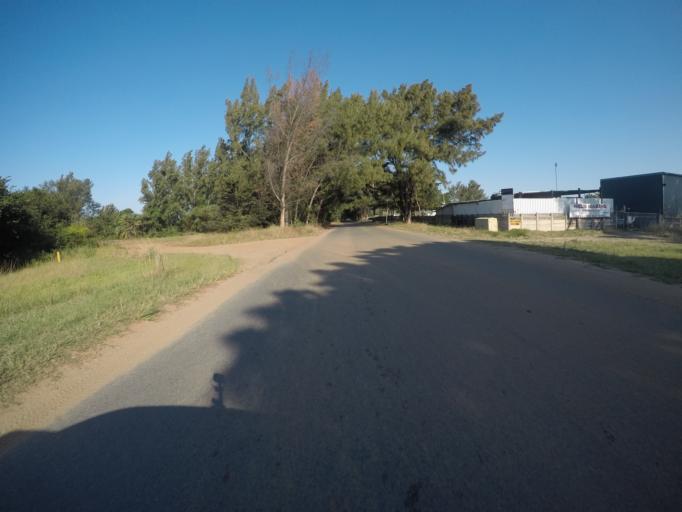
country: ZA
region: KwaZulu-Natal
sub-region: uThungulu District Municipality
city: Richards Bay
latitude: -28.7876
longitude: 32.0835
